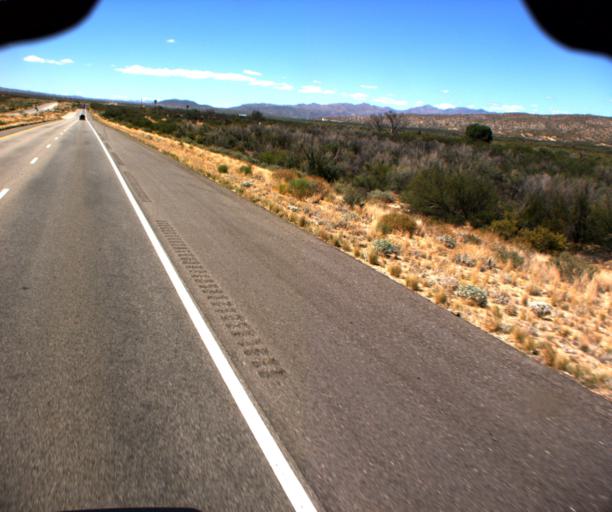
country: US
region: Arizona
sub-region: Yavapai County
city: Bagdad
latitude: 34.8273
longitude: -113.6289
